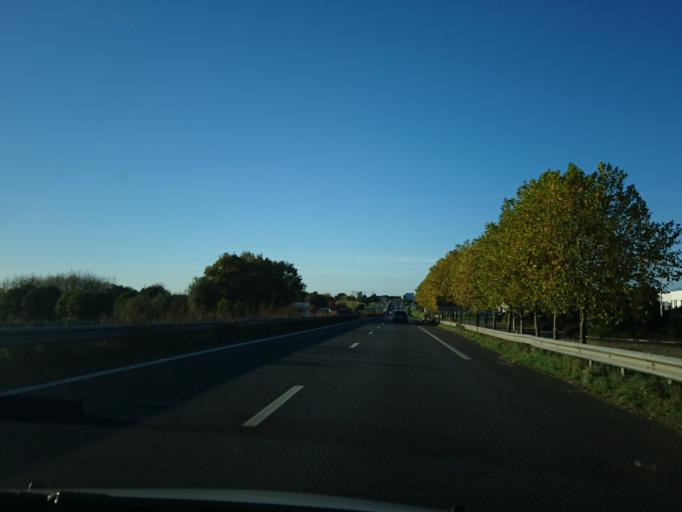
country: FR
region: Brittany
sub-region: Departement des Cotes-d'Armor
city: Lamballe
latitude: 48.4635
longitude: -2.5425
